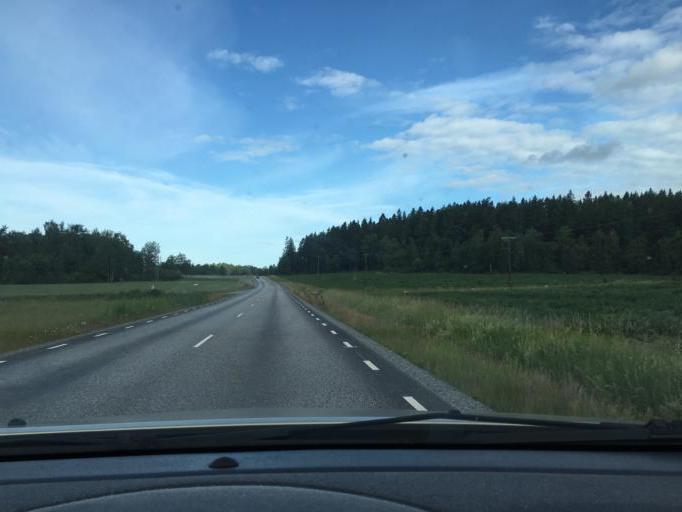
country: SE
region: Stockholm
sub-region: Salems Kommun
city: Ronninge
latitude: 59.2270
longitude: 17.7295
